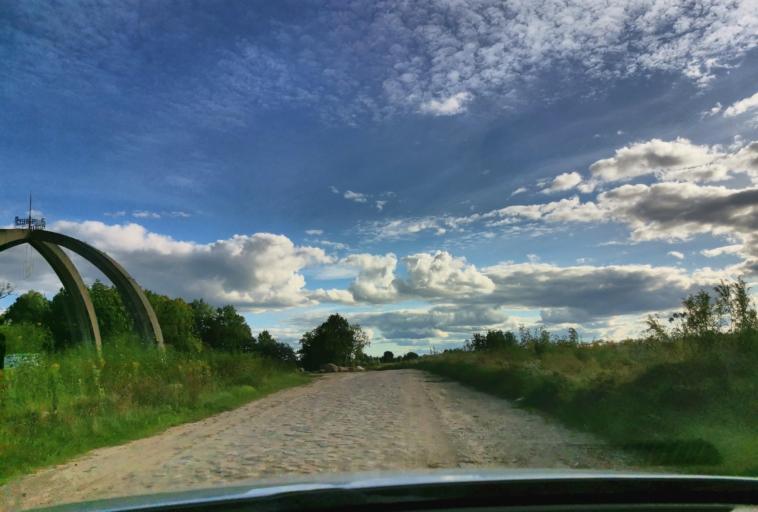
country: RU
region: Kaliningrad
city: Chernyakhovsk
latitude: 54.6371
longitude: 21.7665
